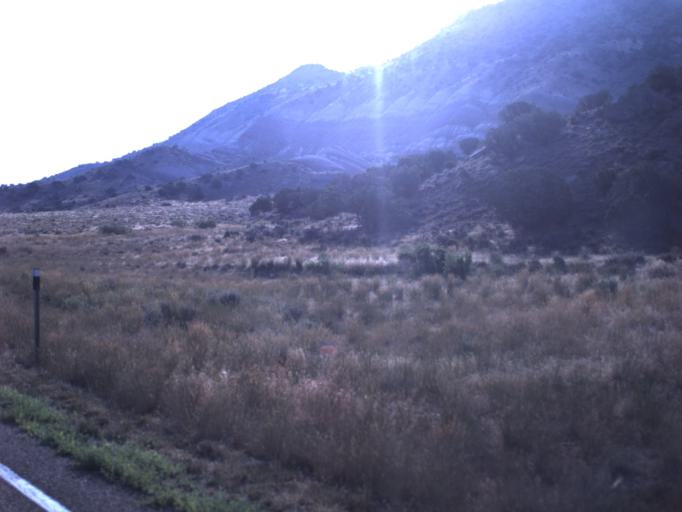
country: US
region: Utah
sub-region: Uintah County
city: Vernal
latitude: 40.5657
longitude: -109.5007
